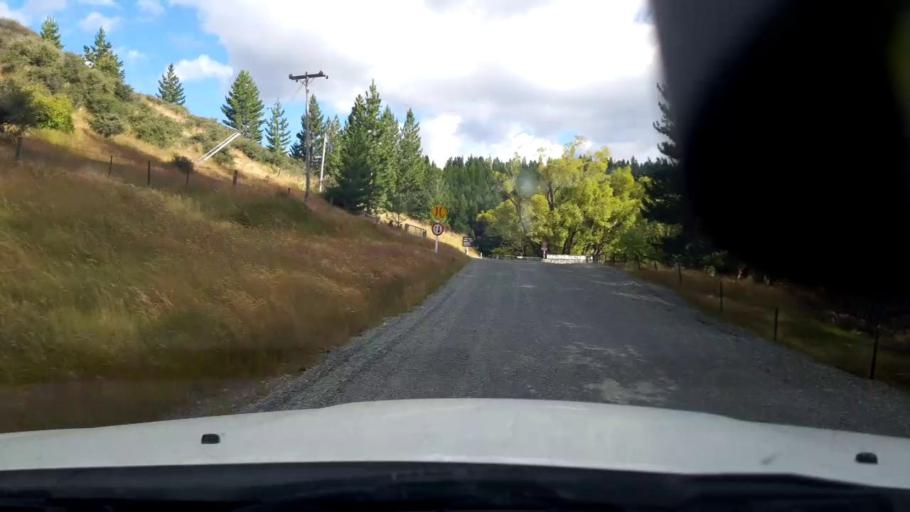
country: NZ
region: Canterbury
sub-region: Timaru District
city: Pleasant Point
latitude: -43.8744
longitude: 170.4634
